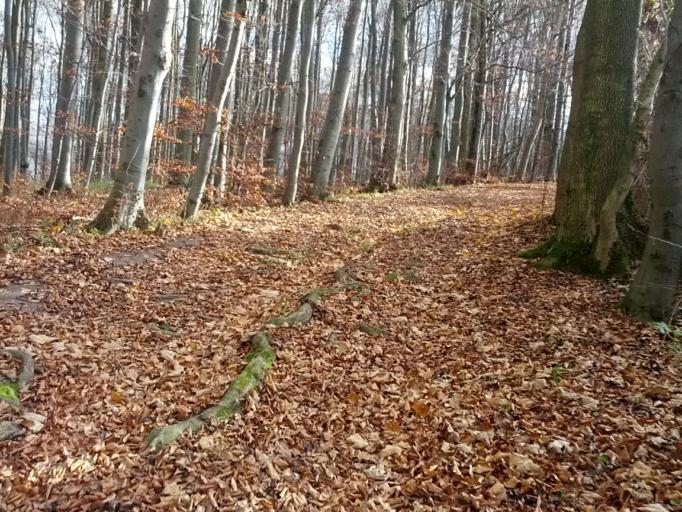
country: DE
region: Thuringia
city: Wolfsburg-Unkeroda
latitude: 50.9733
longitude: 10.2383
